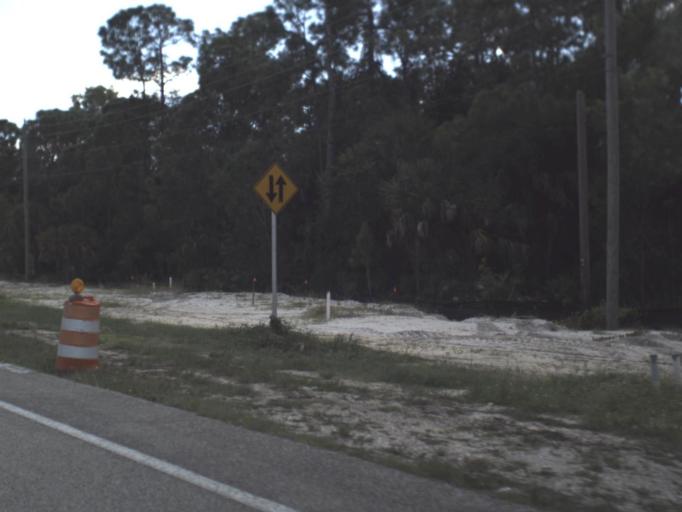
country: US
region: Florida
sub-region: Collier County
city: Lely Resort
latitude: 26.0617
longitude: -81.6970
